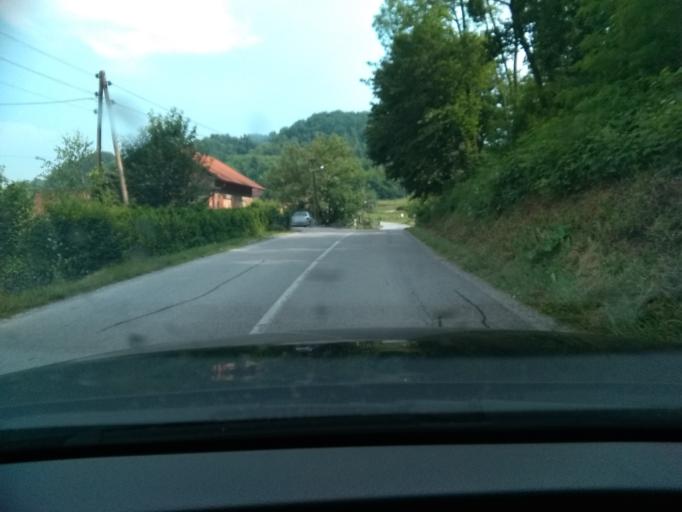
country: HR
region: Krapinsko-Zagorska
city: Pregrada
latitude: 46.0736
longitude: 15.7558
